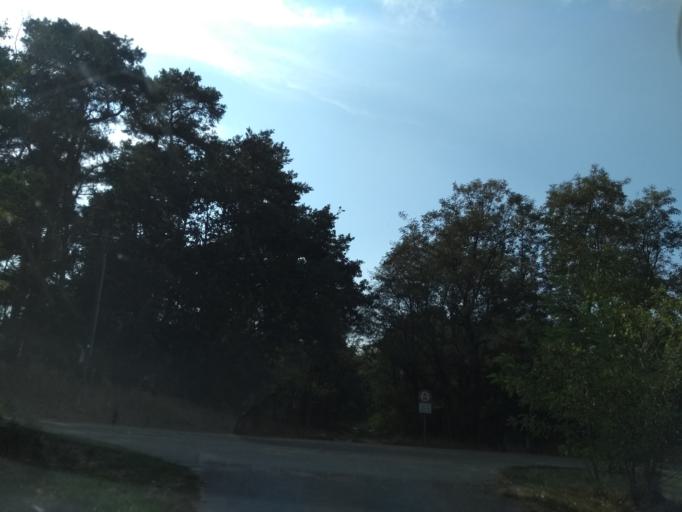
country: DE
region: Brandenburg
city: Luebben
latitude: 51.8670
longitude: 13.8524
